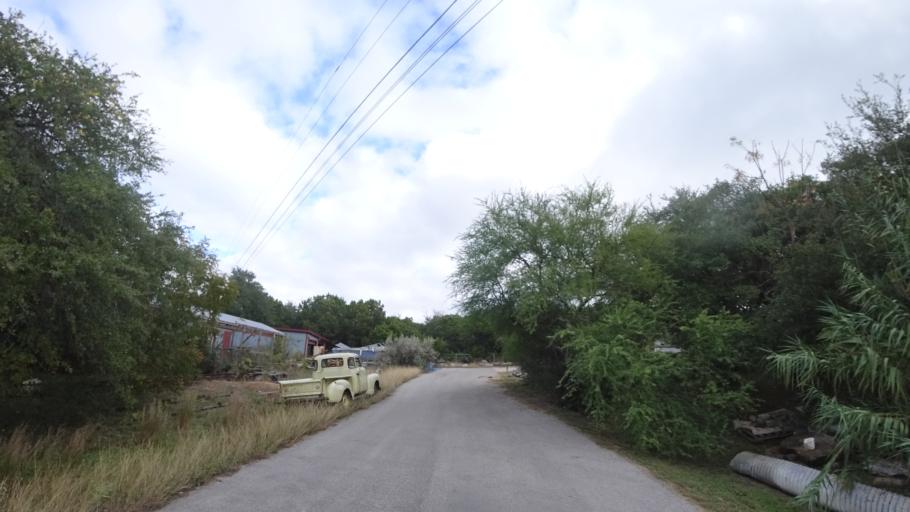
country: US
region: Texas
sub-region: Travis County
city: Bee Cave
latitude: 30.2554
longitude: -97.9259
